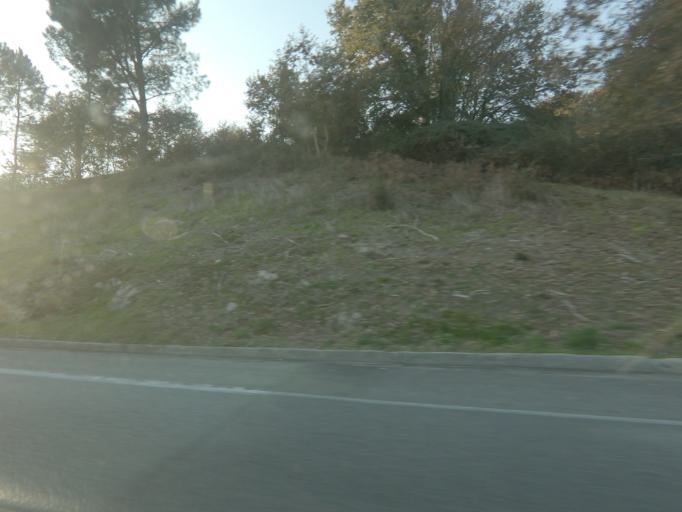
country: PT
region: Porto
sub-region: Marco de Canaveses
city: Marco de Canavezes
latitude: 41.2263
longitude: -8.1330
